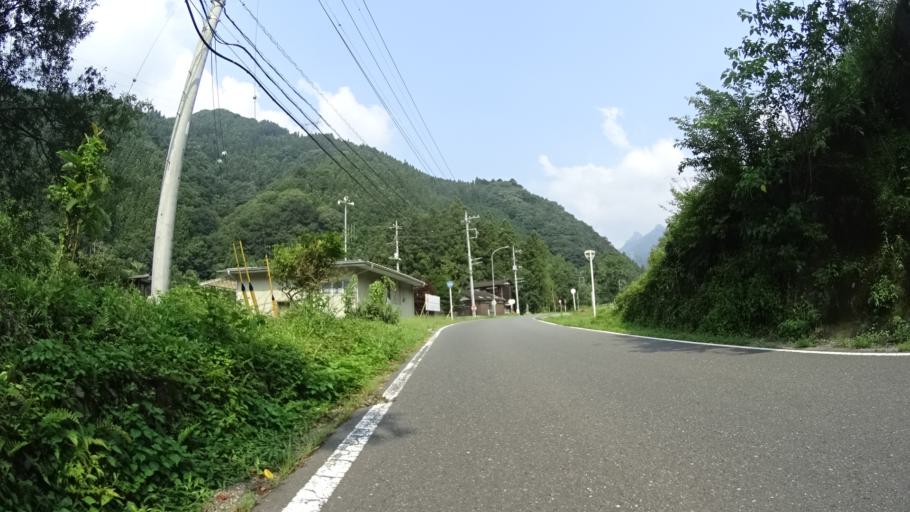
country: JP
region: Saitama
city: Chichibu
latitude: 36.0406
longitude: 138.8954
